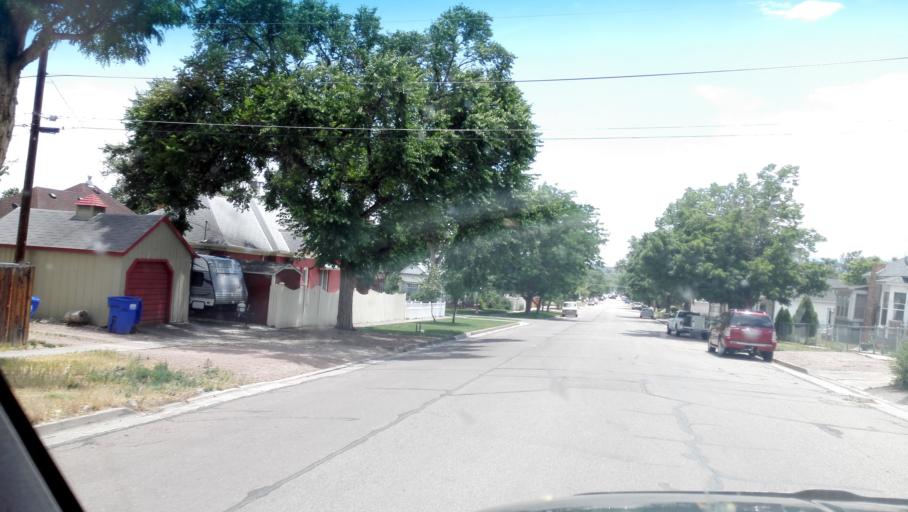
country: US
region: Colorado
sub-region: Fremont County
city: Canon City
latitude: 38.4459
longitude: -105.2448
